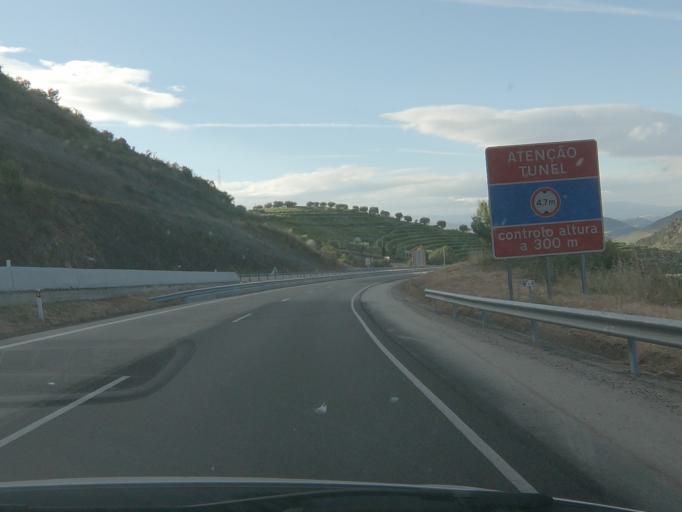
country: PT
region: Viseu
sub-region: Lamego
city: Lamego
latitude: 41.1019
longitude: -7.7761
